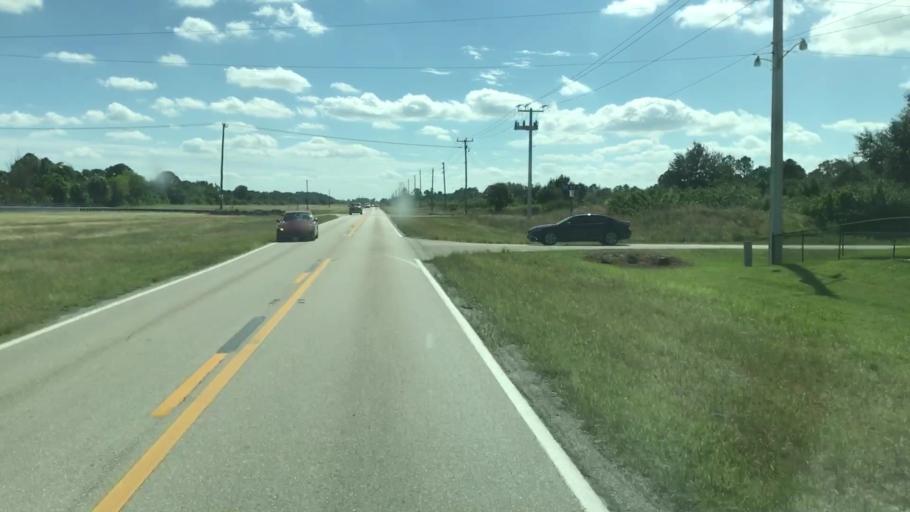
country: US
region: Florida
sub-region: Lee County
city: Lehigh Acres
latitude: 26.6621
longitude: -81.6636
